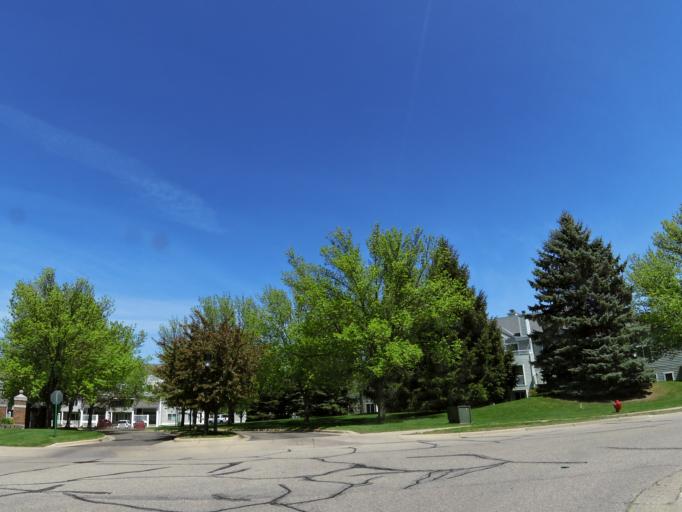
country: US
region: Minnesota
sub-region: Scott County
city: Savage
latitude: 44.8176
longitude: -93.3838
